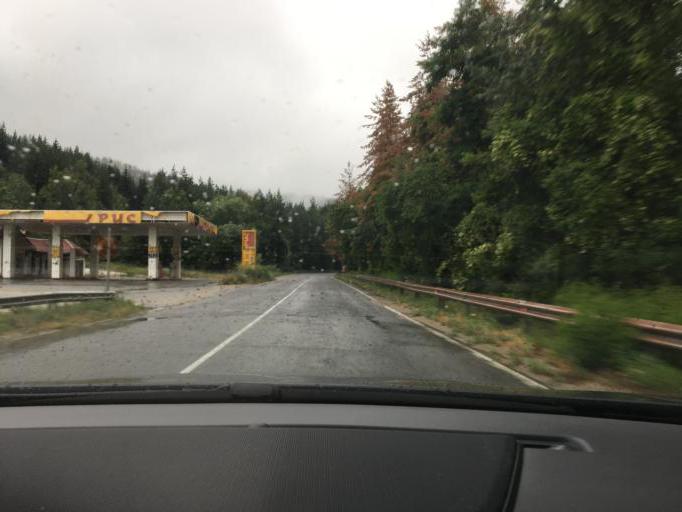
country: MK
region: Kriva Palanka
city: Kriva Palanka
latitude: 42.2252
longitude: 22.4809
